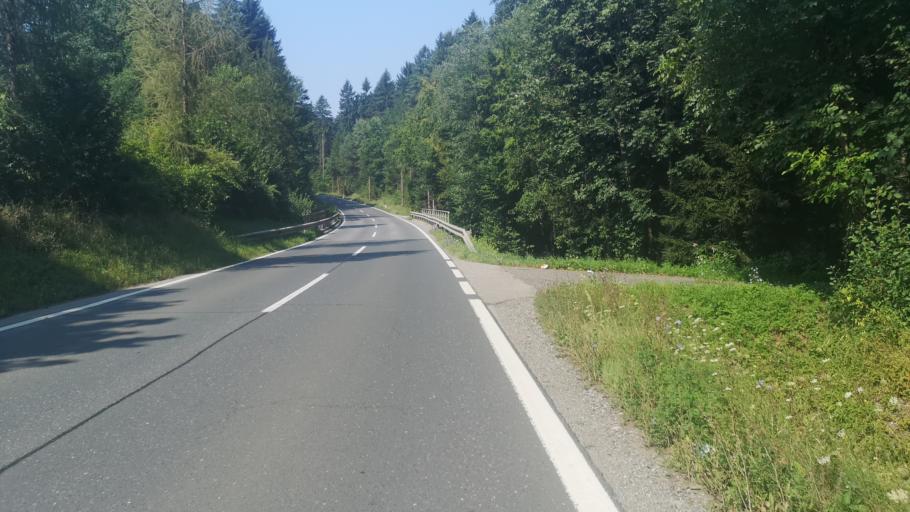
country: AT
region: Styria
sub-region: Politischer Bezirk Graz-Umgebung
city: Unterpremstatten
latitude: 46.9743
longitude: 15.3843
